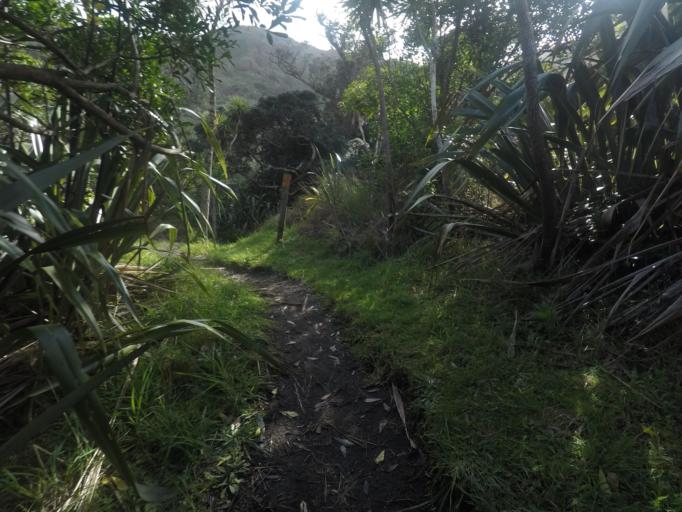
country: NZ
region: Auckland
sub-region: Auckland
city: Muriwai Beach
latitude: -36.8829
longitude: 174.4399
